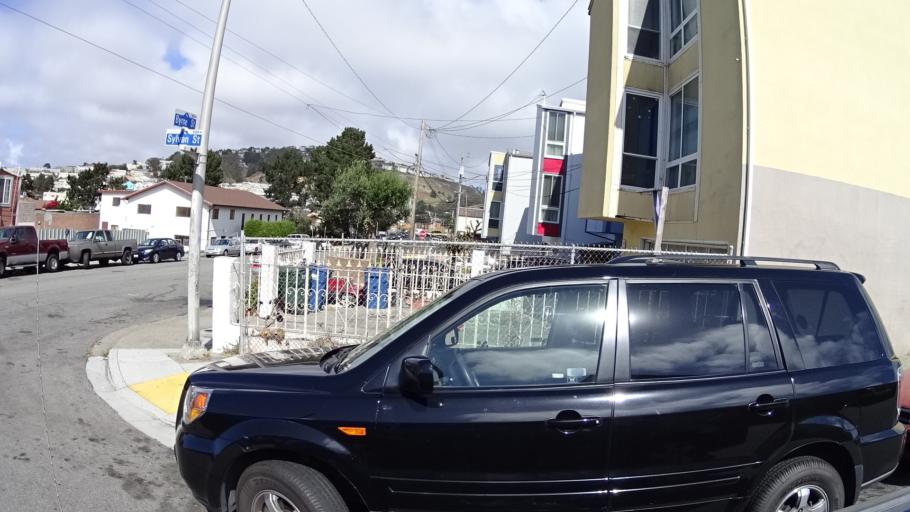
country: US
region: California
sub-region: San Mateo County
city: Colma
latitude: 37.6882
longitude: -122.4601
